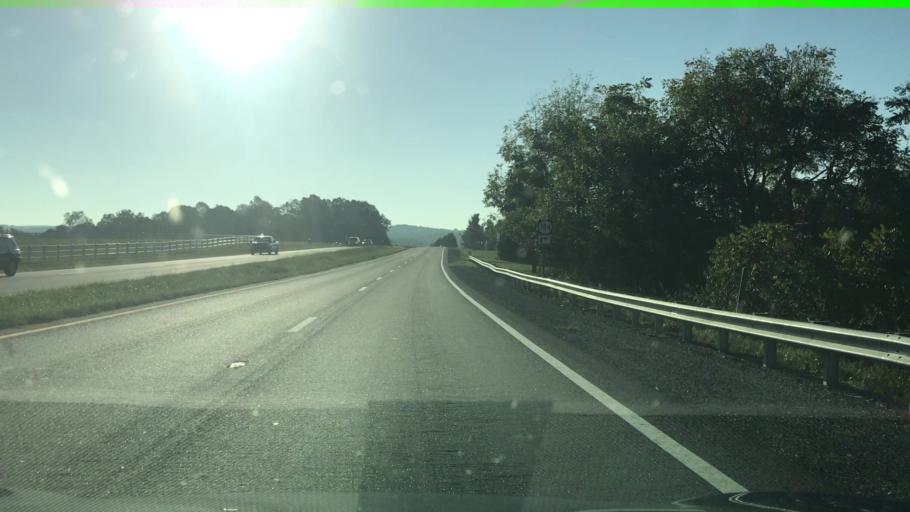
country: US
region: Virginia
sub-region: City of Bedford
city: Bedford
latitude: 37.3147
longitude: -79.4092
